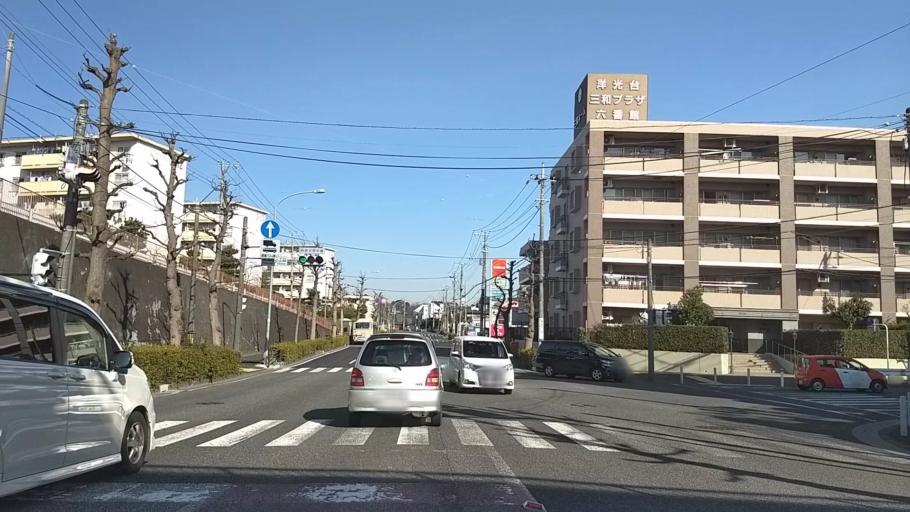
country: JP
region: Kanagawa
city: Yokohama
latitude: 35.3834
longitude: 139.5924
